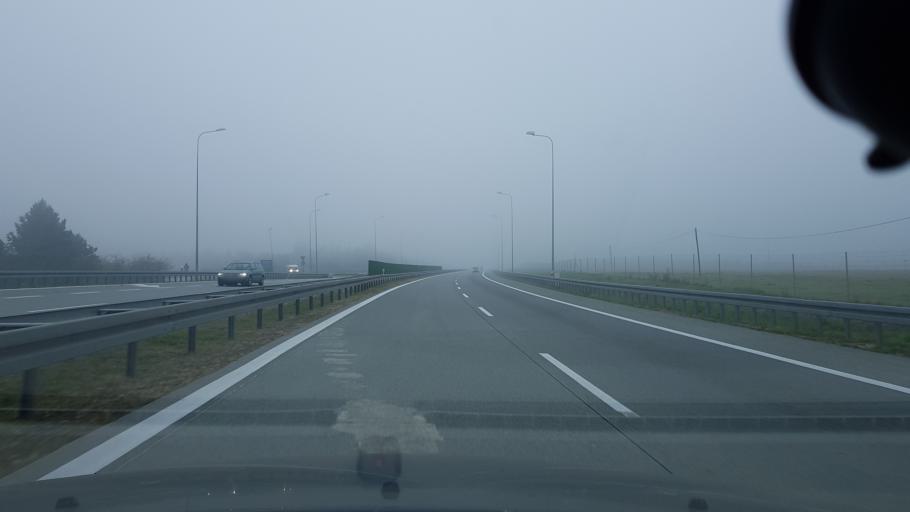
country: PL
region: Lodz Voivodeship
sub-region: Powiat skierniewicki
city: Kowiesy
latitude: 51.8634
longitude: 20.3825
